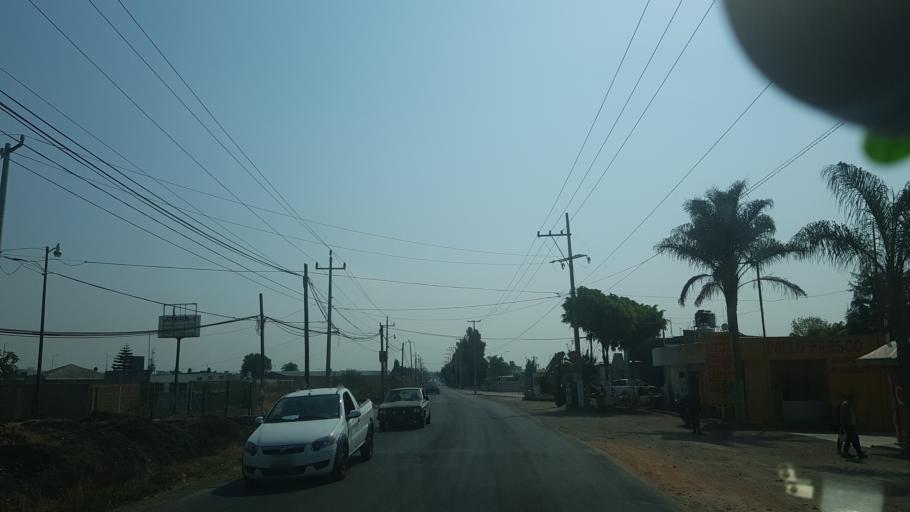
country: MX
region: Puebla
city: Cholula
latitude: 19.0556
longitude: -98.3279
